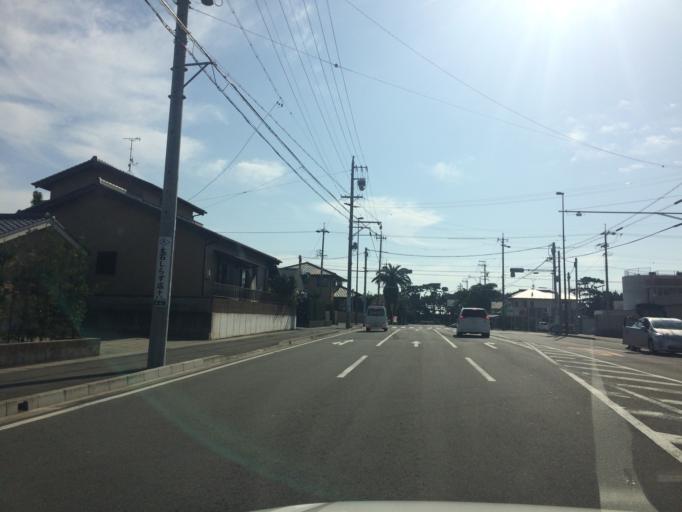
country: JP
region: Shizuoka
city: Shizuoka-shi
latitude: 34.9456
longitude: 138.4128
